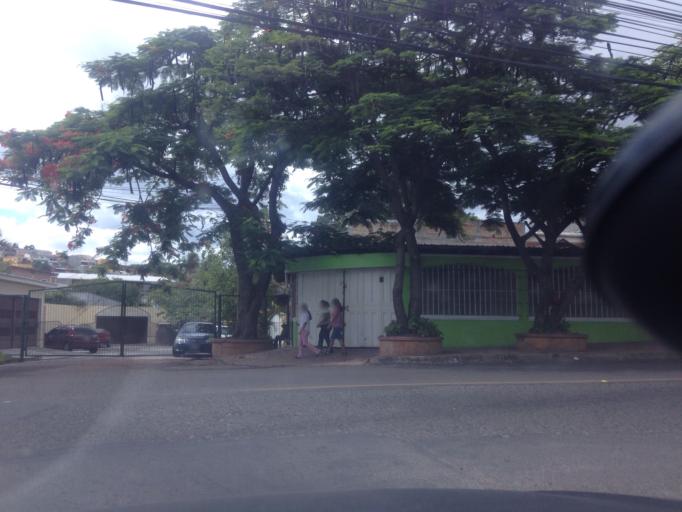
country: HN
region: Francisco Morazan
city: Tegucigalpa
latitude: 14.0769
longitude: -87.1899
